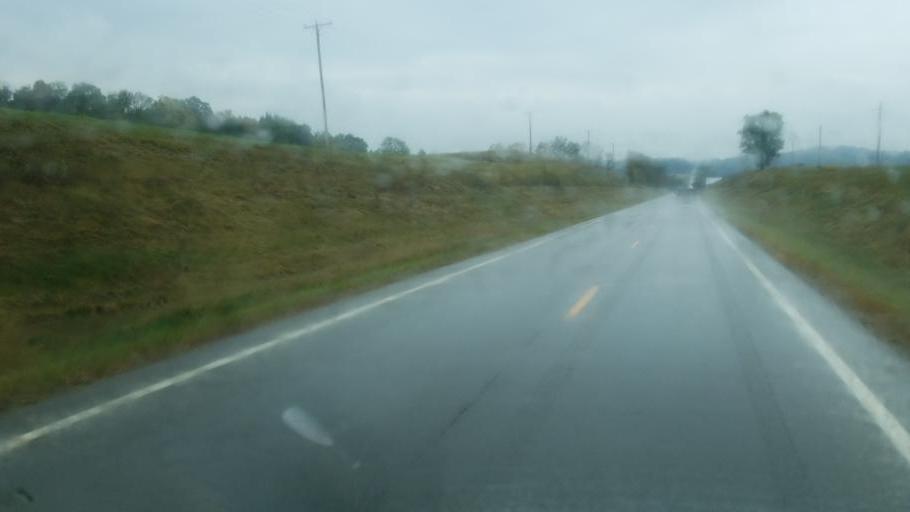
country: US
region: Ohio
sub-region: Richland County
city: Lincoln Heights
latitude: 40.7078
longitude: -82.3785
